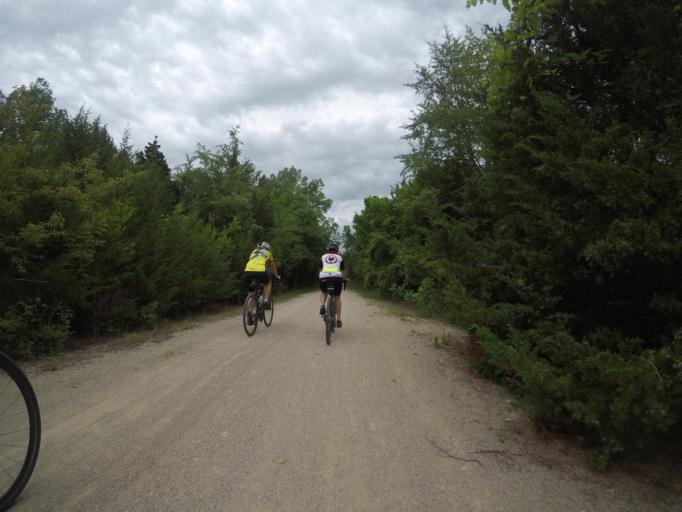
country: US
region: Kansas
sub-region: Anderson County
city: Garnett
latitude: 38.2646
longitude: -95.2462
